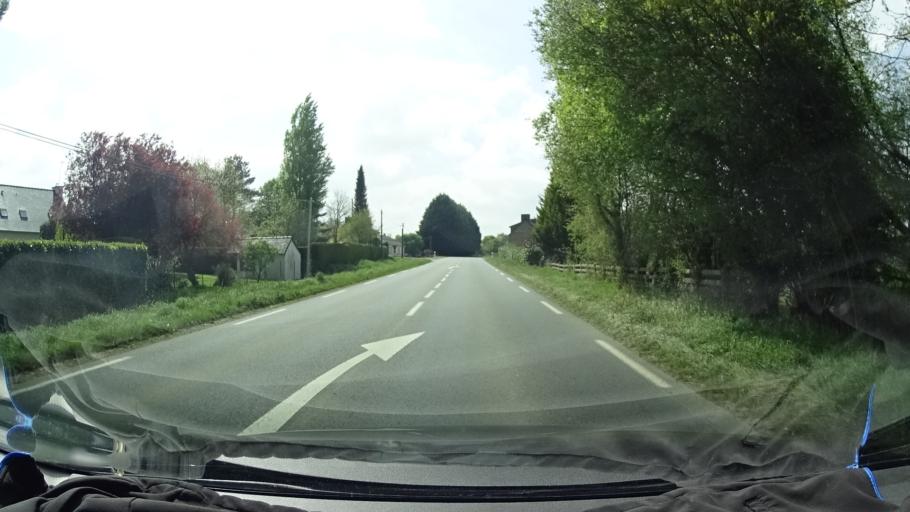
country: FR
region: Brittany
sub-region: Departement des Cotes-d'Armor
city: Saint-Agathon
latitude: 48.5807
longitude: -3.0637
